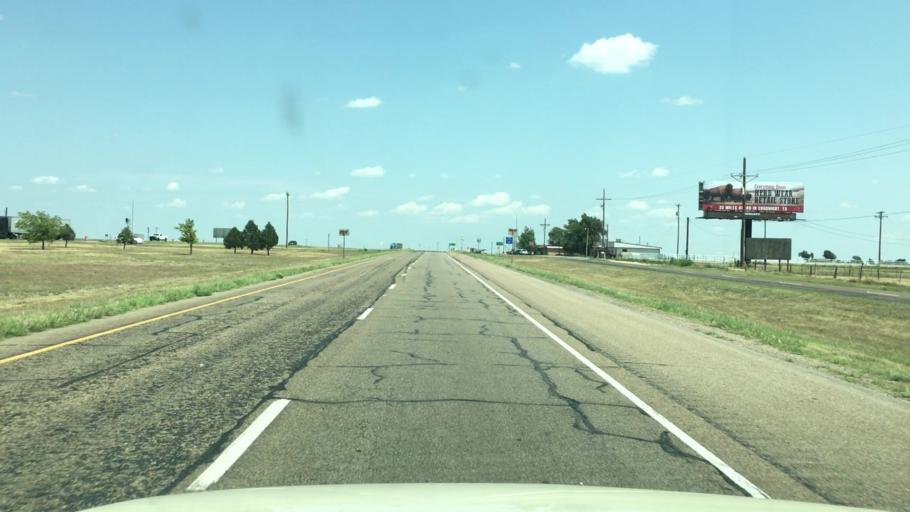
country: US
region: Texas
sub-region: Potter County
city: Amarillo
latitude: 35.1928
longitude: -101.6912
